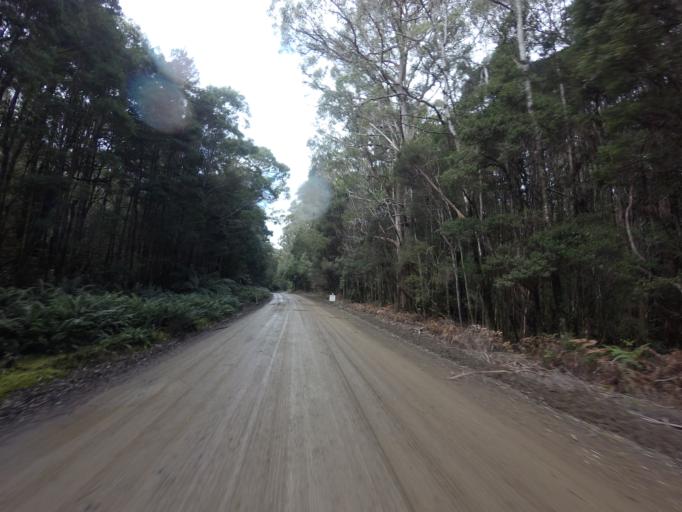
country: AU
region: Tasmania
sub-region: Huon Valley
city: Geeveston
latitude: -43.4016
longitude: 146.8628
